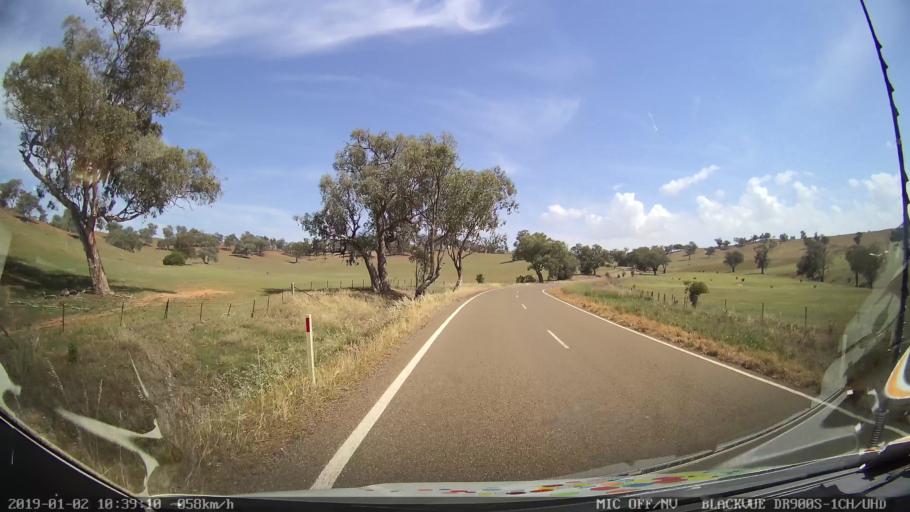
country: AU
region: New South Wales
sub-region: Gundagai
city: Gundagai
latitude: -34.8133
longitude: 148.3198
